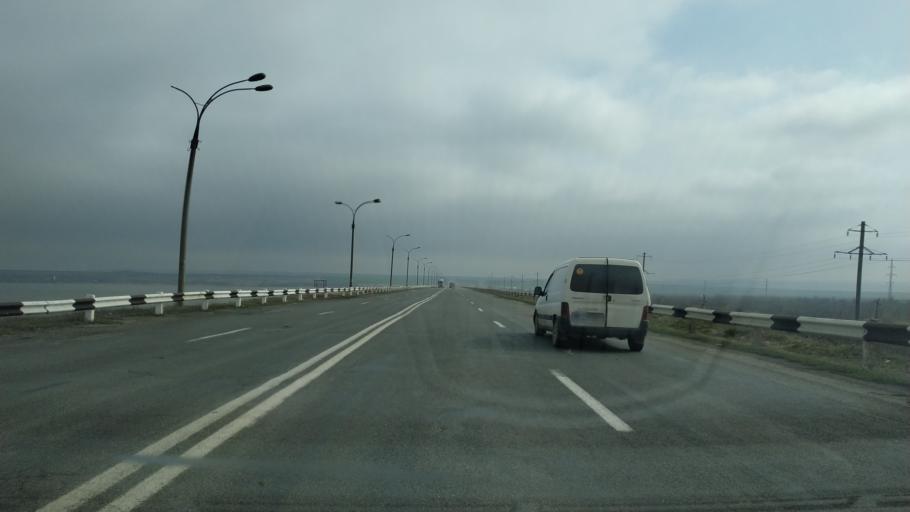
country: MD
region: Straseni
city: Taraclia
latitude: 45.9375
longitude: 28.5963
